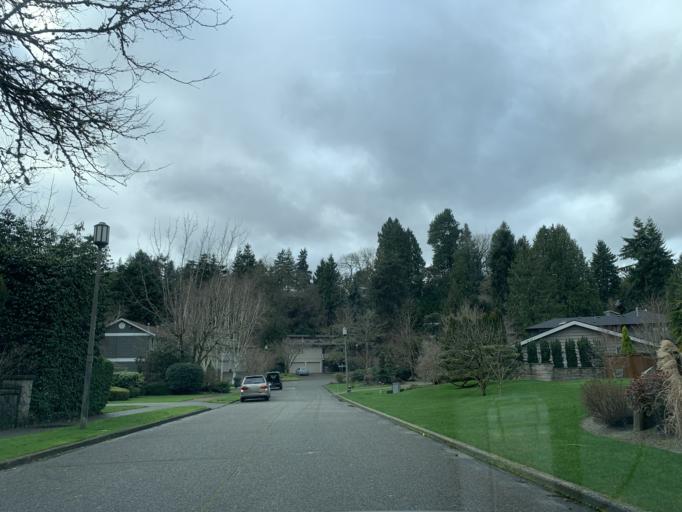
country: US
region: Washington
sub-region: King County
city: Yarrow Point
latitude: 47.6670
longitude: -122.2691
